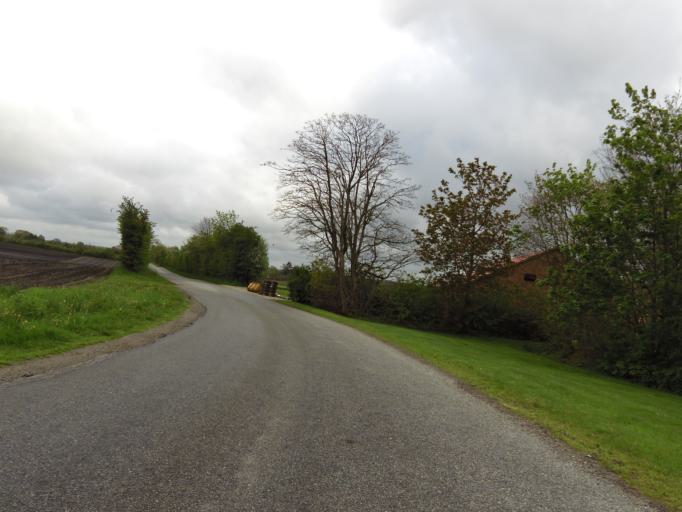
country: DK
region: South Denmark
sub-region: Haderslev Kommune
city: Gram
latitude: 55.2836
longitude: 8.9738
